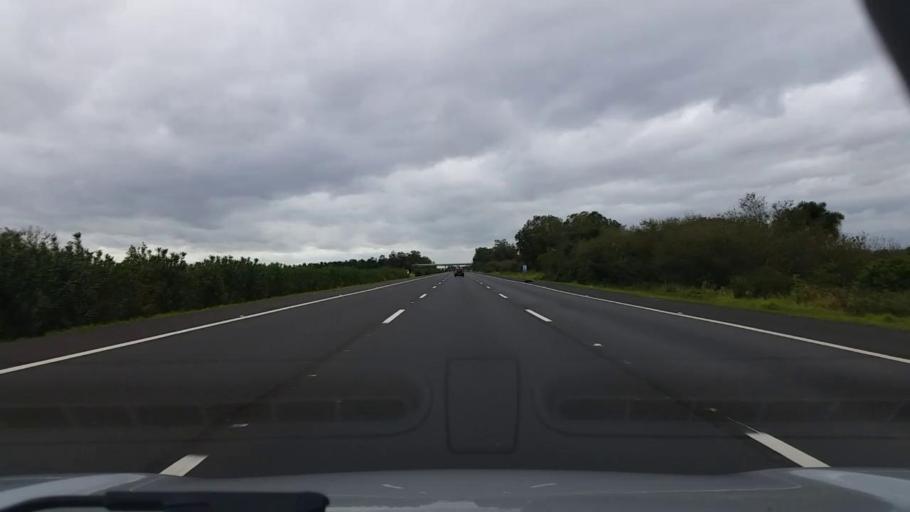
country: BR
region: Rio Grande do Sul
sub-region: Rolante
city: Rolante
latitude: -29.8844
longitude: -50.5712
